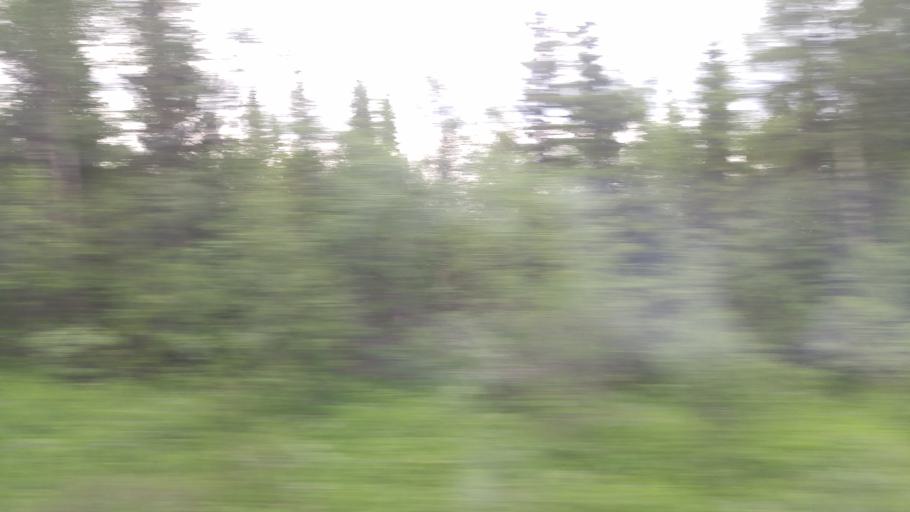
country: SE
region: Jaemtland
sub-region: Are Kommun
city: Are
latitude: 63.3160
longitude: 12.5047
